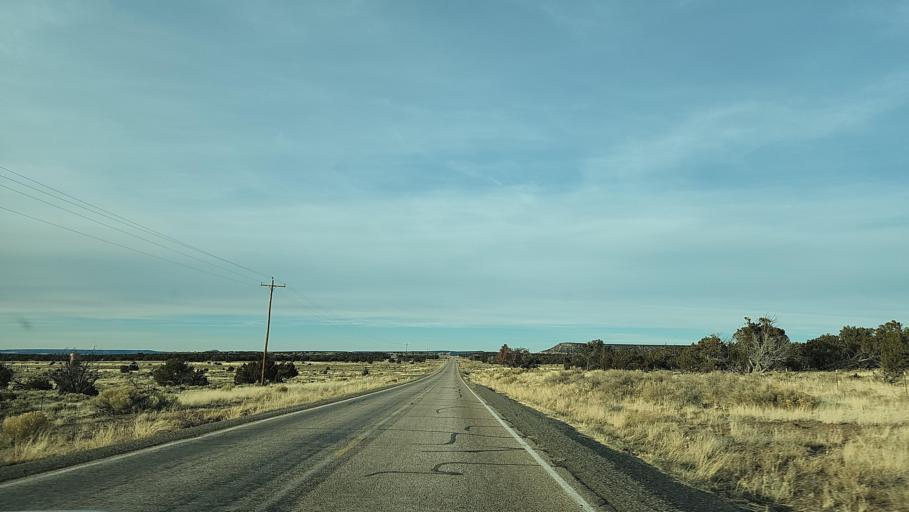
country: US
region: New Mexico
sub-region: McKinley County
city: Black Rock
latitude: 34.4391
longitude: -108.4274
